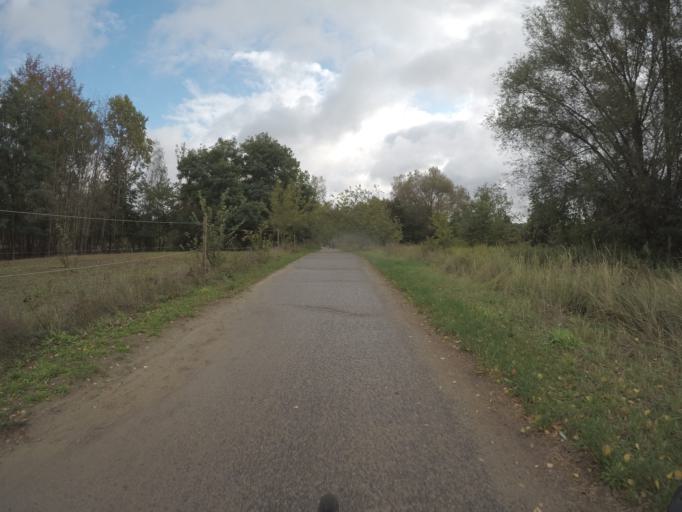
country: DE
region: Berlin
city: Lubars
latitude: 52.6265
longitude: 13.3664
